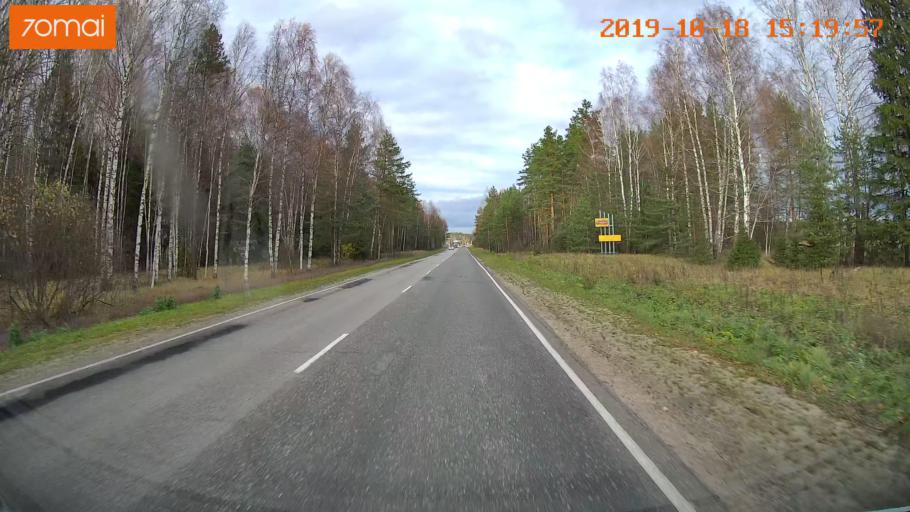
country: RU
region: Vladimir
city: Anopino
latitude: 55.6807
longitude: 40.7415
